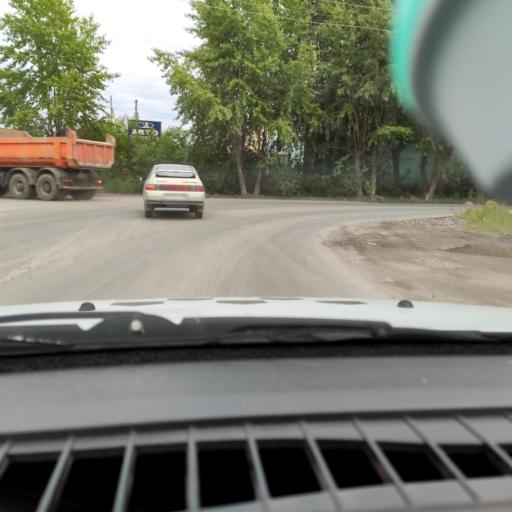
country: RU
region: Perm
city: Chusovoy
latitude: 58.2991
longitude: 57.8142
